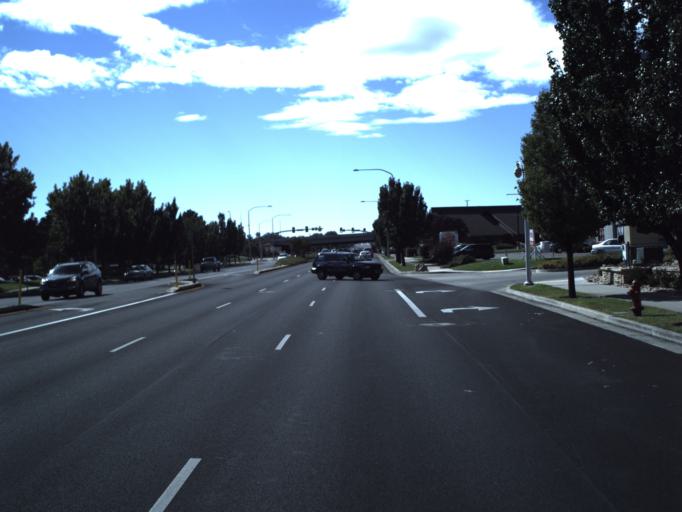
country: US
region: Utah
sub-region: Salt Lake County
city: Taylorsville
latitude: 40.6485
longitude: -111.9390
